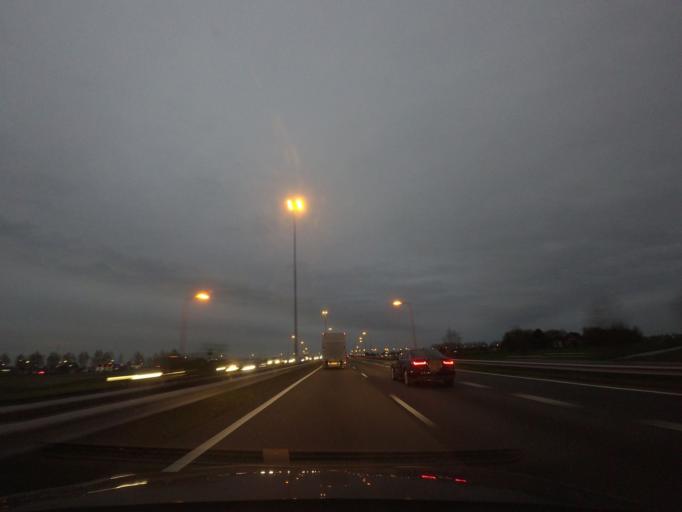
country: NL
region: South Holland
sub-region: Gemeente Gorinchem
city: Gorinchem
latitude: 51.9018
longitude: 4.9801
